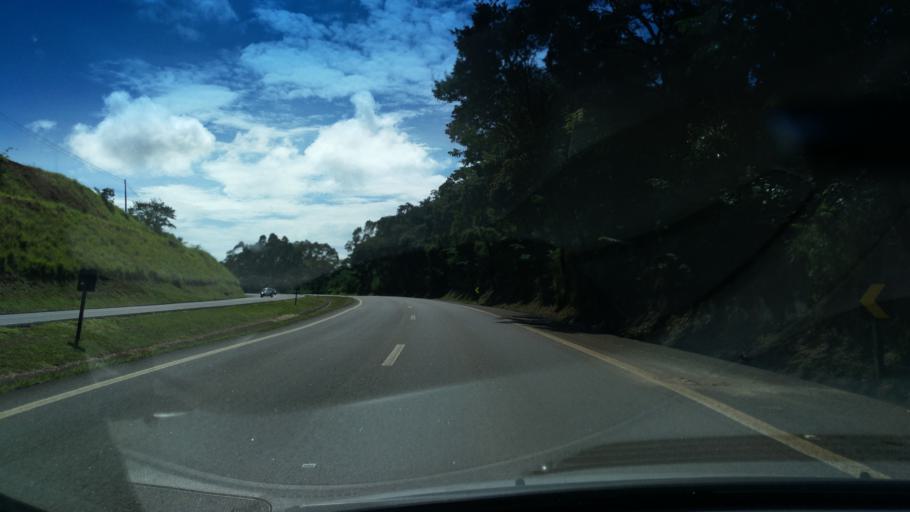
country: BR
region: Sao Paulo
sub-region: Santo Antonio Do Jardim
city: Espirito Santo do Pinhal
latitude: -22.2198
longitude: -46.7877
